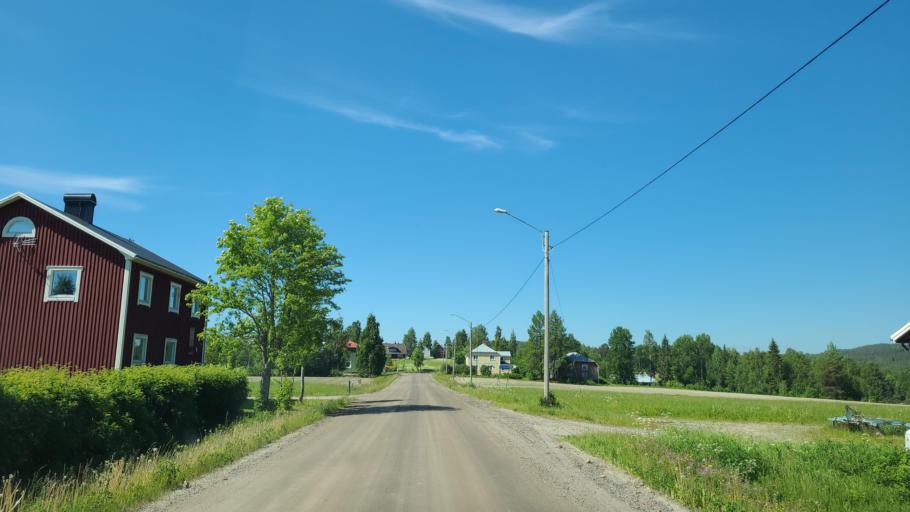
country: SE
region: Vaesterbotten
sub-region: Bjurholms Kommun
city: Bjurholm
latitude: 63.6682
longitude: 19.0067
